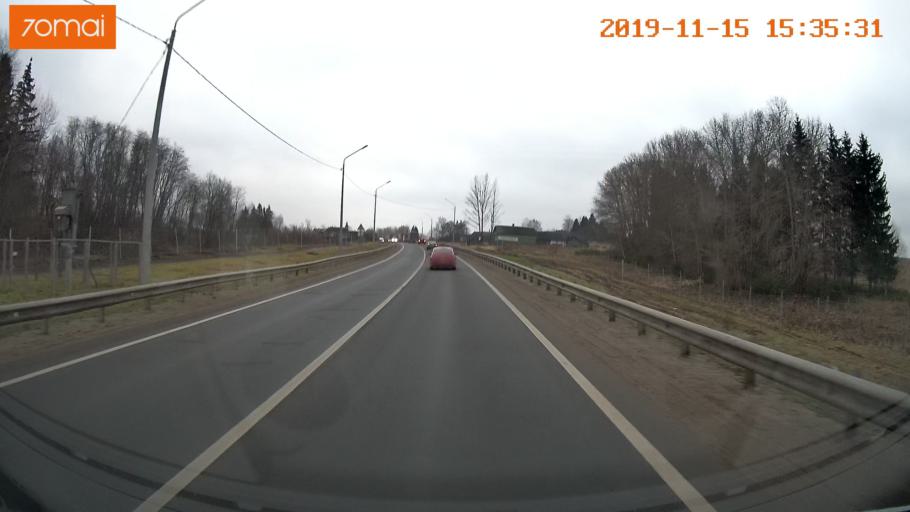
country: RU
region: Jaroslavl
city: Danilov
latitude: 58.0582
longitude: 40.0874
